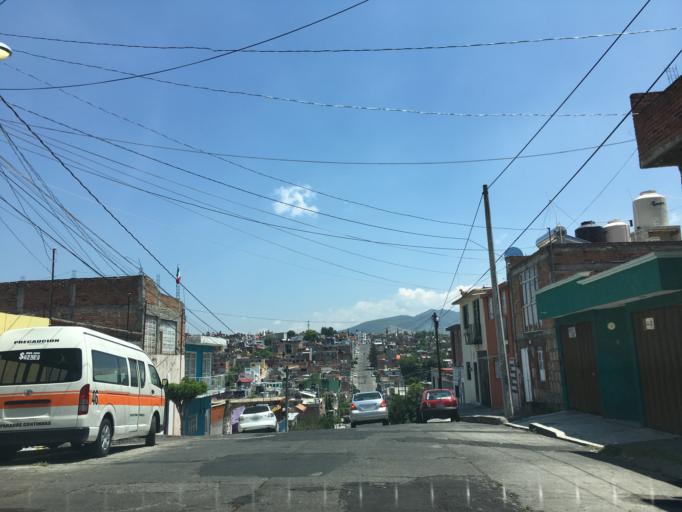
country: MX
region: Michoacan
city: Morelia
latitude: 19.7082
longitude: -101.1812
